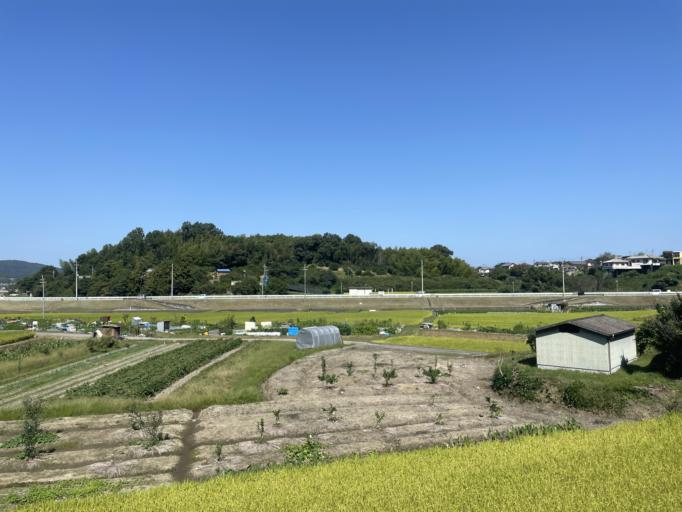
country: JP
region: Nara
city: Tawaramoto
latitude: 34.5865
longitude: 135.7288
